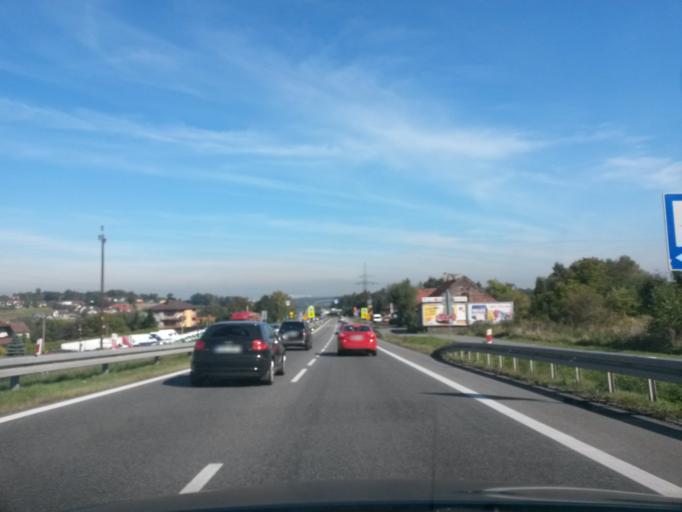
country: PL
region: Lesser Poland Voivodeship
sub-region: Powiat krakowski
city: Libertow
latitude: 49.9619
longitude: 19.8928
